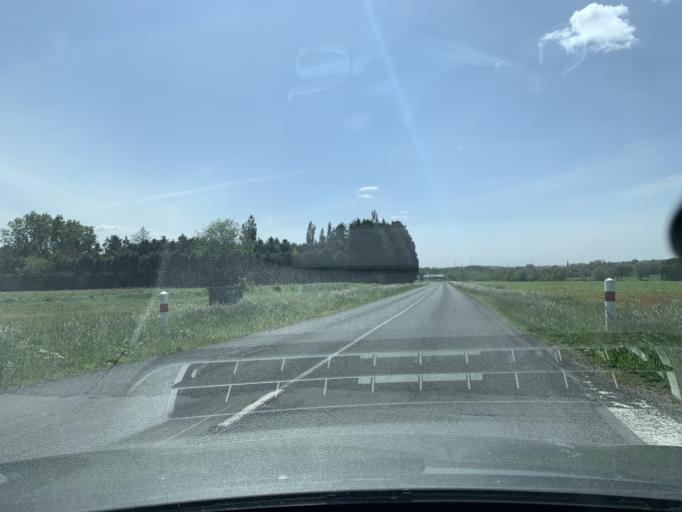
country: FR
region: Nord-Pas-de-Calais
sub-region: Departement du Nord
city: Rumilly-en-Cambresis
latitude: 50.1359
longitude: 3.1993
